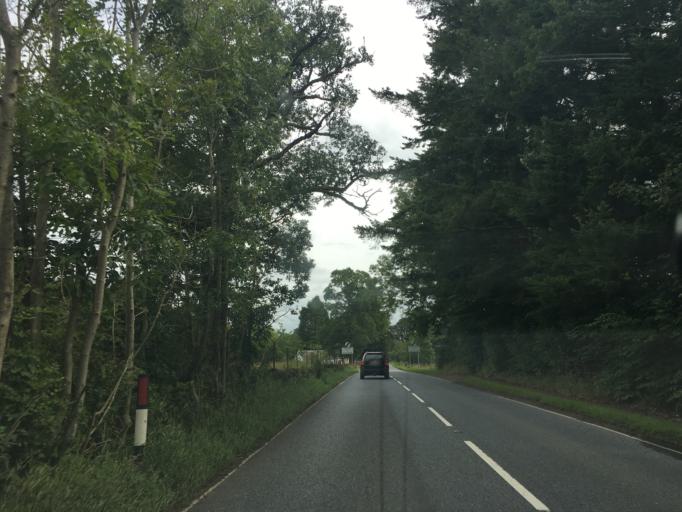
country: GB
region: Scotland
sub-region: Stirling
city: Callander
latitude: 56.2463
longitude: -4.2395
